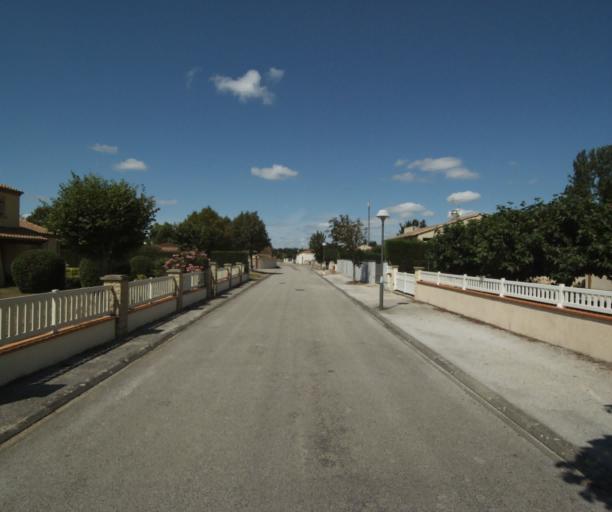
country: FR
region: Midi-Pyrenees
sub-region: Departement de la Haute-Garonne
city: Revel
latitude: 43.4619
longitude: 2.0172
